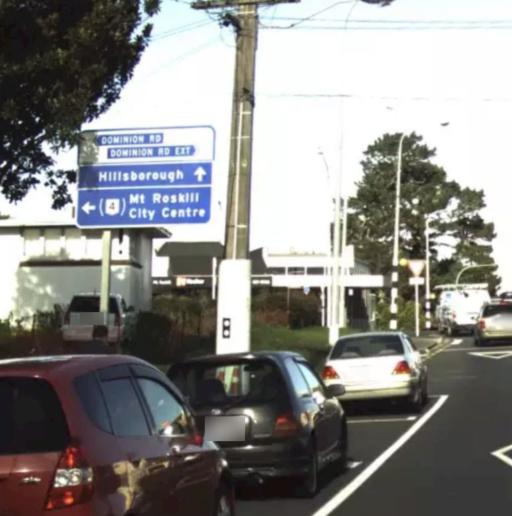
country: NZ
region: Auckland
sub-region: Auckland
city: Auckland
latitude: -36.9200
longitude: 174.7356
